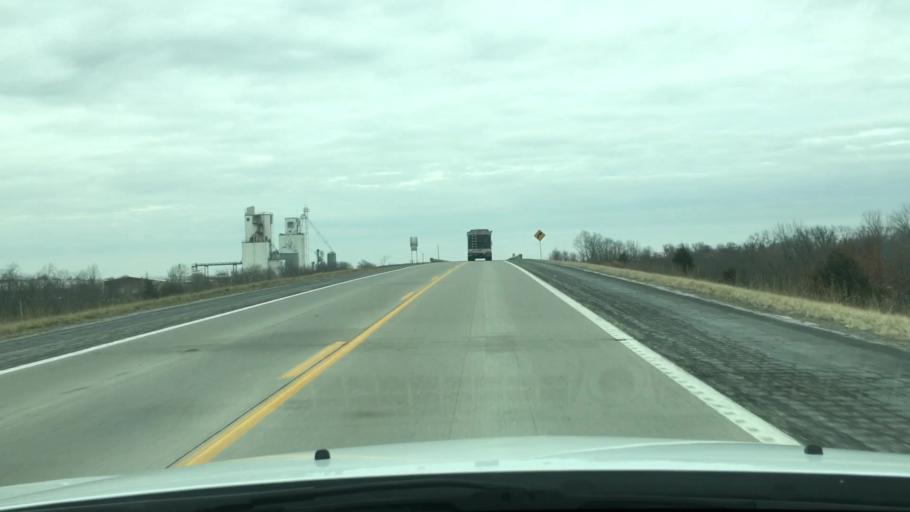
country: US
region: Missouri
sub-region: Audrain County
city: Mexico
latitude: 39.1551
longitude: -91.8431
